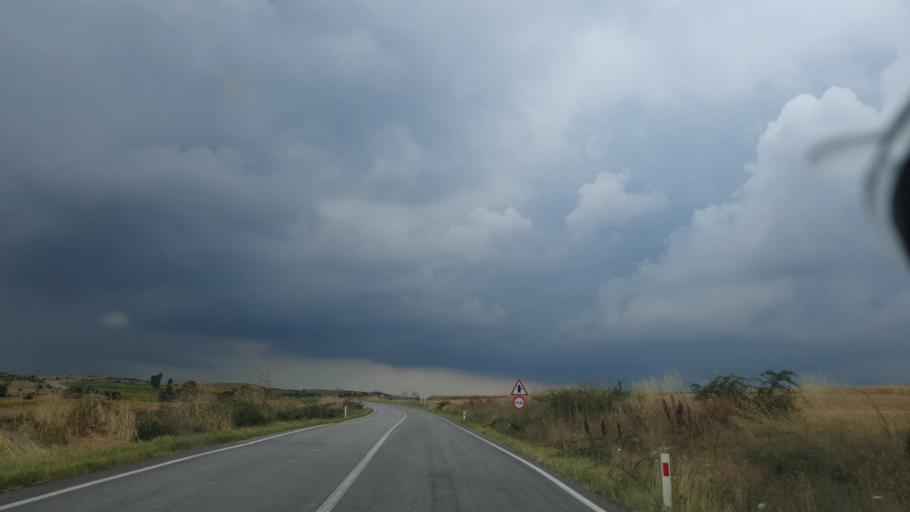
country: TR
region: Tekirdag
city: Hayrabolu
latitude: 41.2283
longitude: 27.0329
